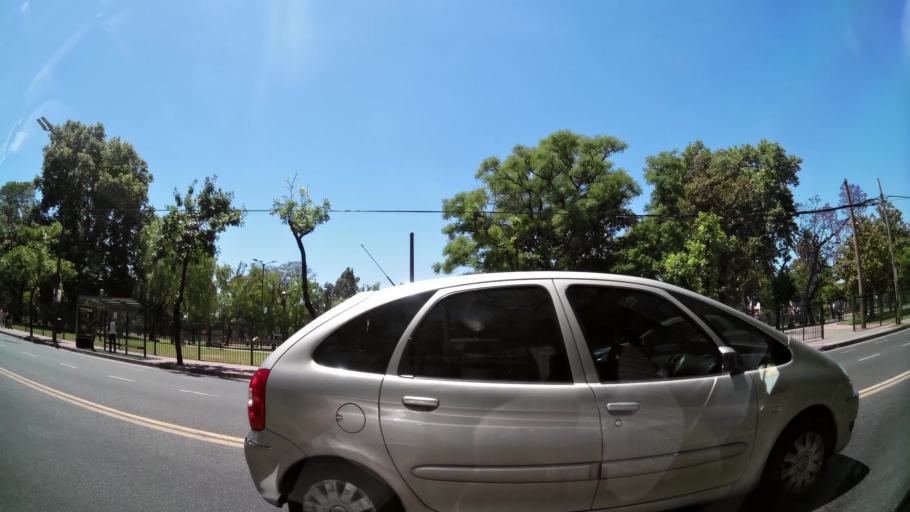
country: AR
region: Buenos Aires
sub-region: Partido de Avellaneda
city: Avellaneda
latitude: -34.6506
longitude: -58.3891
